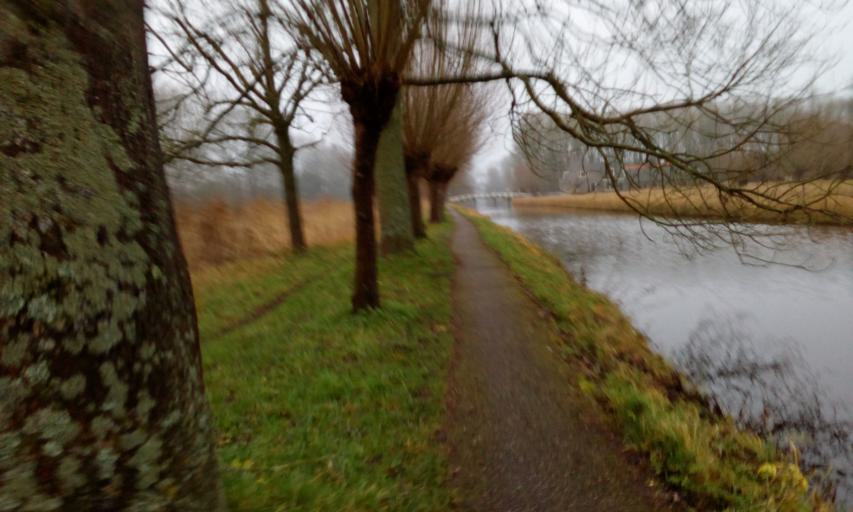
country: NL
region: South Holland
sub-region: Gemeente Den Haag
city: Ypenburg
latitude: 52.0261
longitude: 4.3785
